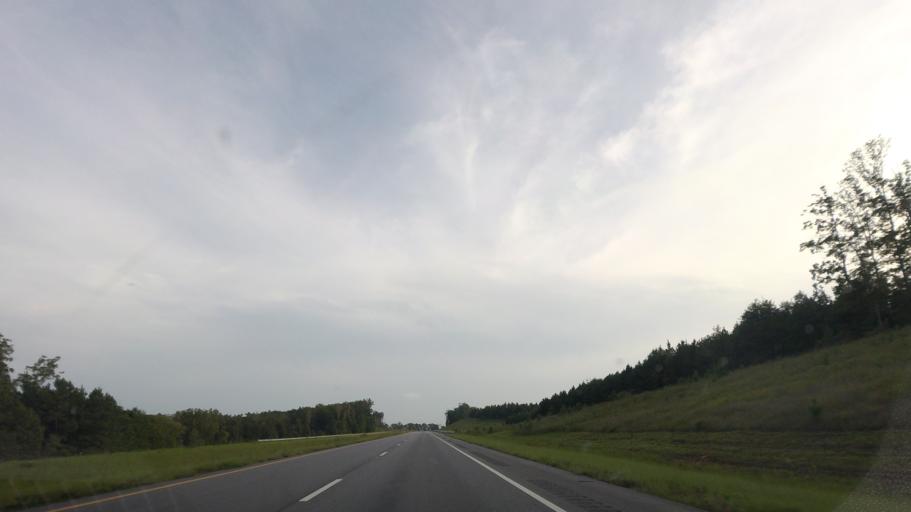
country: US
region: Georgia
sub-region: Wilkinson County
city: Gordon
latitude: 32.8660
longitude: -83.3773
